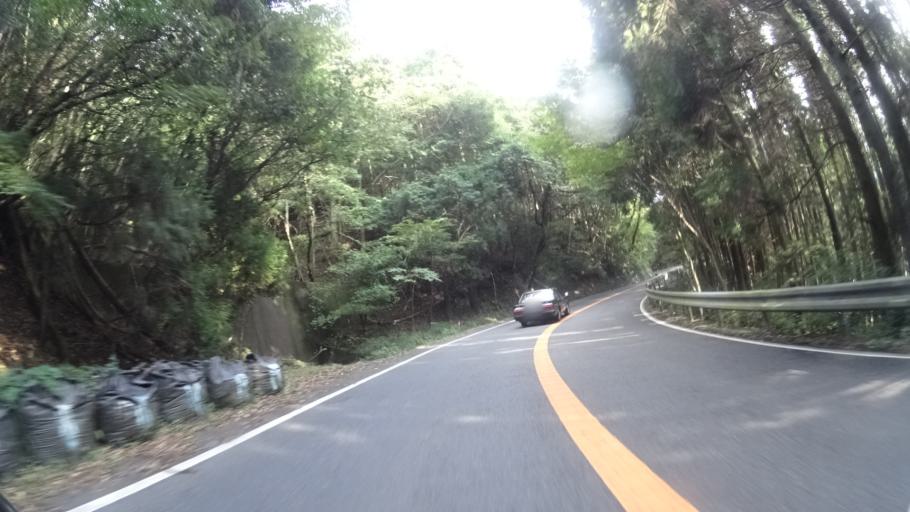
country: JP
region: Oita
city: Beppu
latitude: 33.2652
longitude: 131.3715
